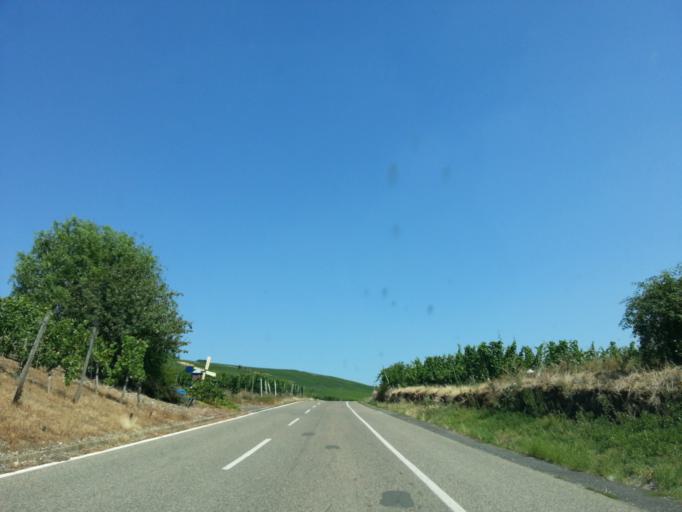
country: DE
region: Rheinland-Pfalz
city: Minheim
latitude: 49.8688
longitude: 6.9379
